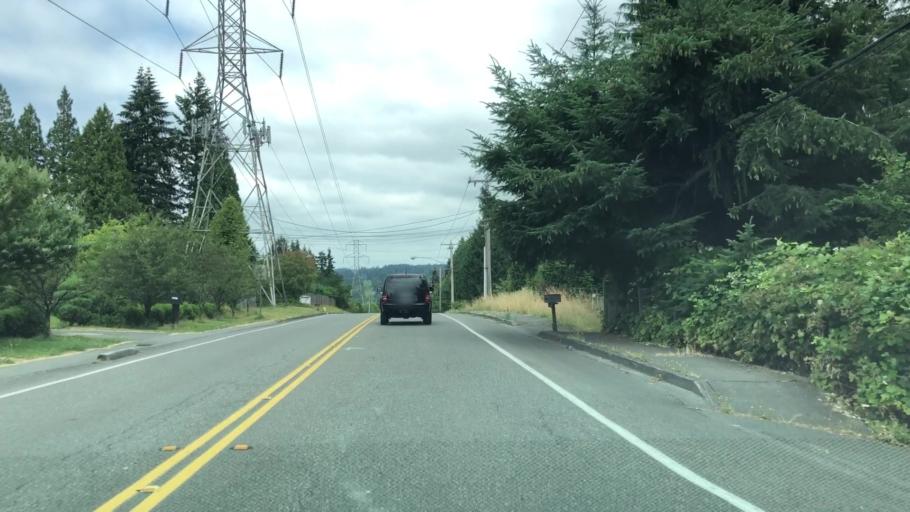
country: US
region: Washington
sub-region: King County
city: Woodinville
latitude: 47.7456
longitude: -122.1748
